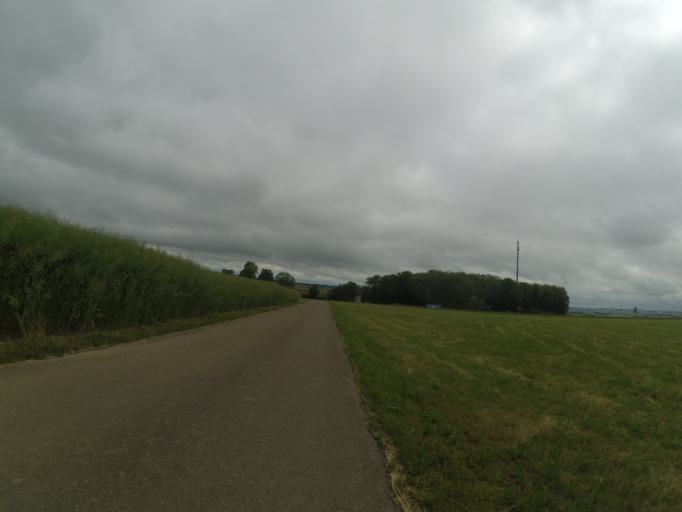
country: DE
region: Baden-Wuerttemberg
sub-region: Tuebingen Region
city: Bernstadt
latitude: 48.4780
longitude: 10.0533
